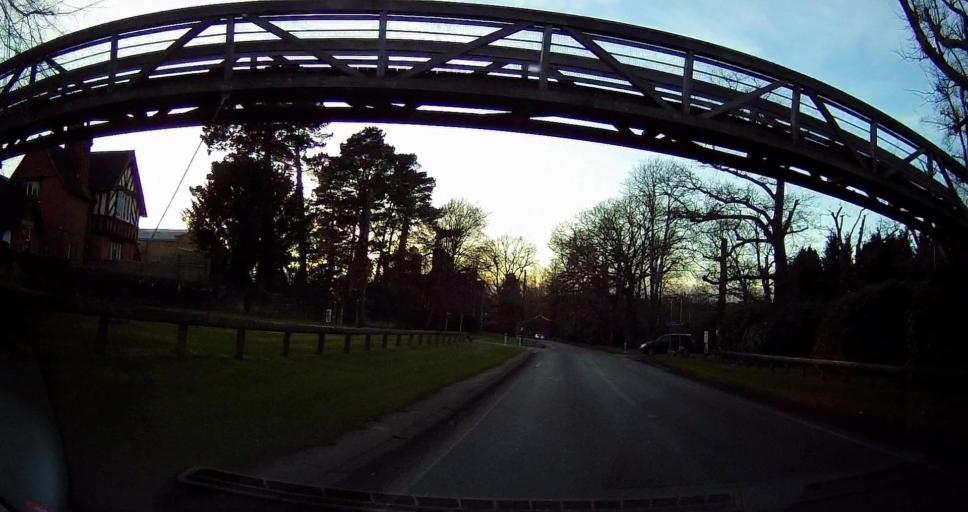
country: GB
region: England
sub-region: West Sussex
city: Maidenbower
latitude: 51.0944
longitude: -0.1193
